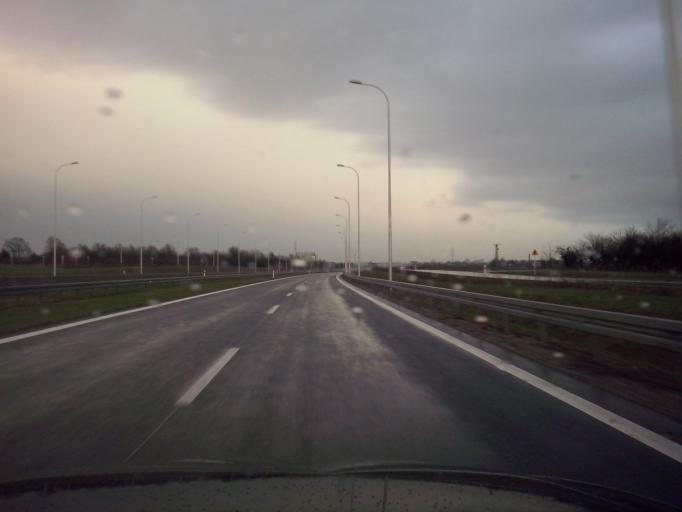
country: PL
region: Lublin Voivodeship
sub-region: Powiat lubelski
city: Jastkow
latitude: 51.2775
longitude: 22.4705
